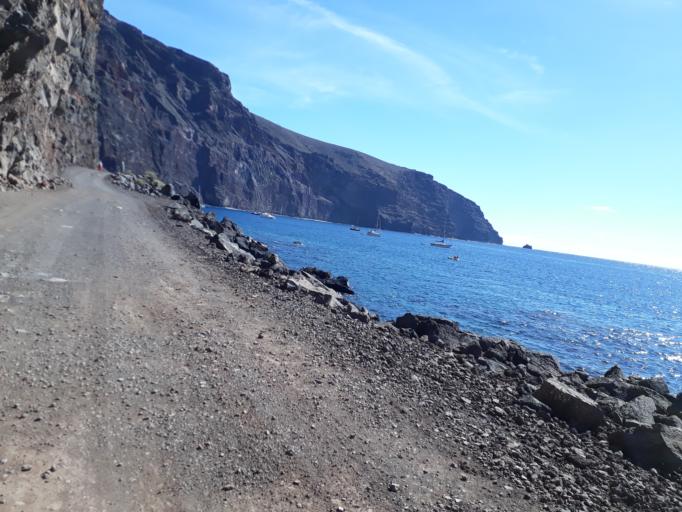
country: ES
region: Canary Islands
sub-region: Provincia de Santa Cruz de Tenerife
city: Alajero
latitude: 28.0809
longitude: -17.3295
